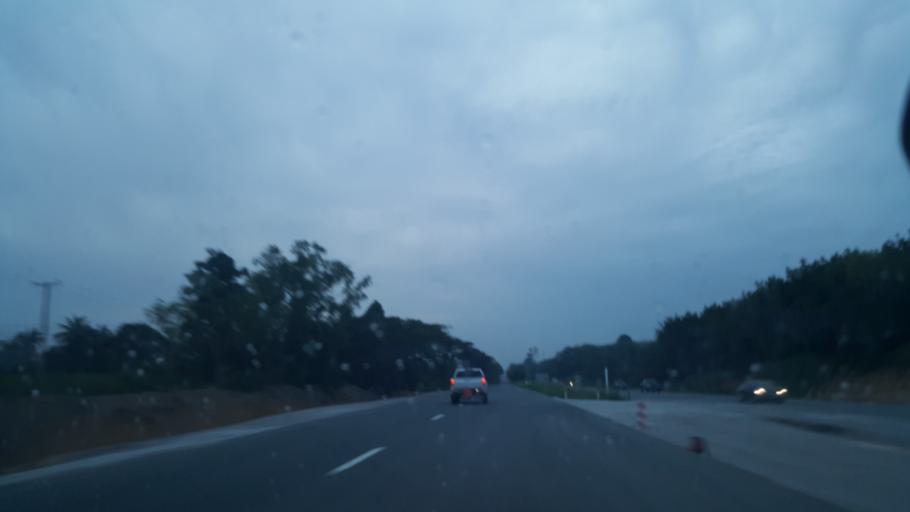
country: TH
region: Rayong
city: Ban Chang
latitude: 12.7929
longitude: 100.9920
